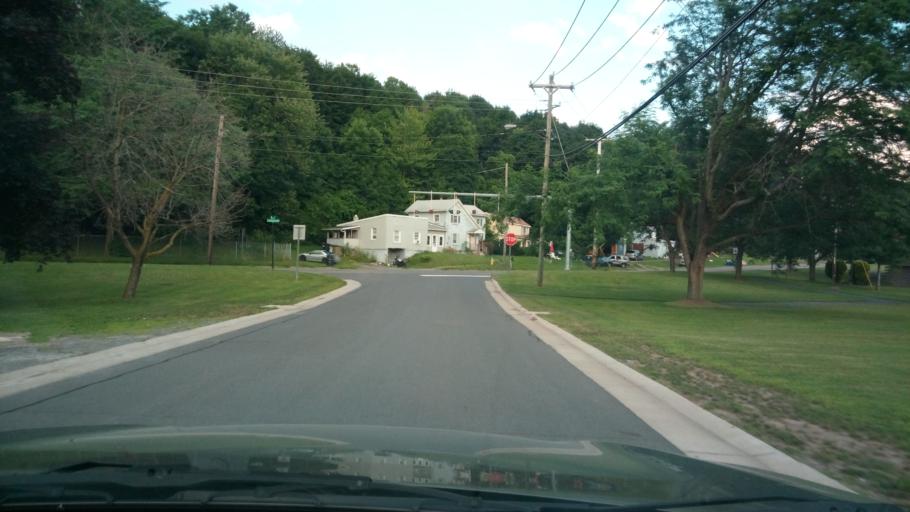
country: US
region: New York
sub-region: Wayne County
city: Clyde
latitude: 43.0824
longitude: -76.8675
